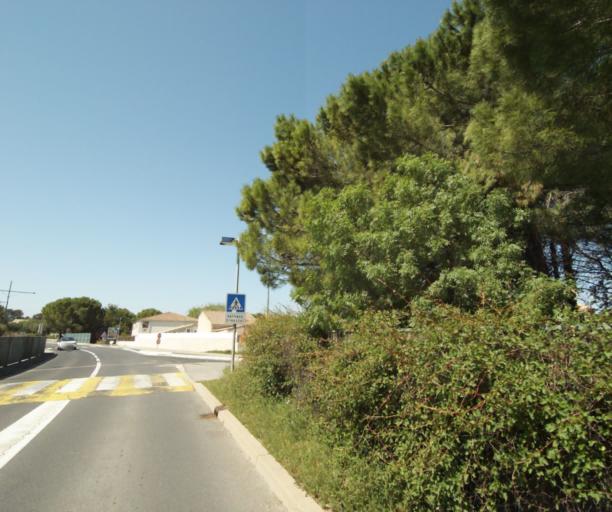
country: FR
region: Languedoc-Roussillon
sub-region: Departement de l'Herault
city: Clapiers
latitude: 43.6536
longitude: 3.8838
